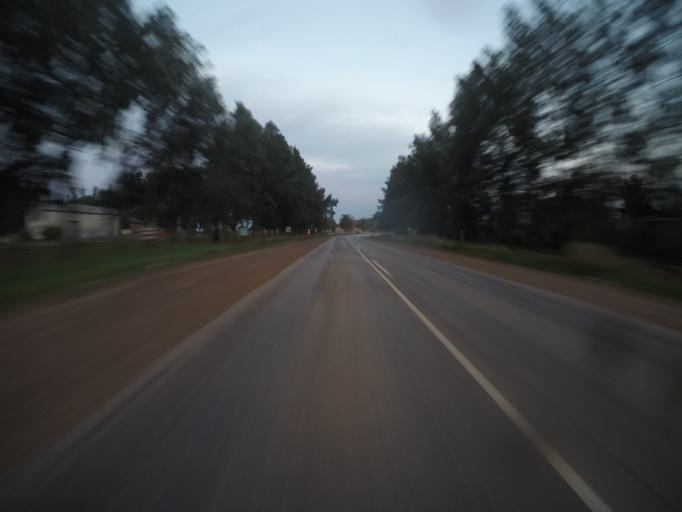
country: ZA
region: Western Cape
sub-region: Eden District Municipality
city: Plettenberg Bay
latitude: -33.8021
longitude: 23.6645
